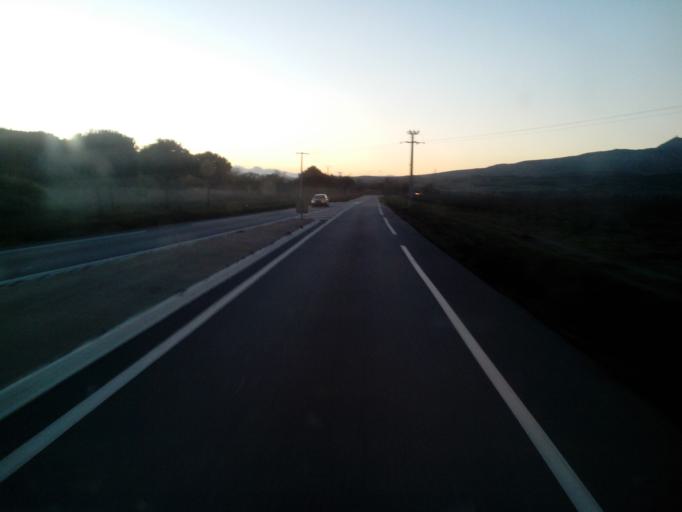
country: FR
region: Languedoc-Roussillon
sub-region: Departement des Pyrenees-Orientales
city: Baixas
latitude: 42.7791
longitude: 2.8148
